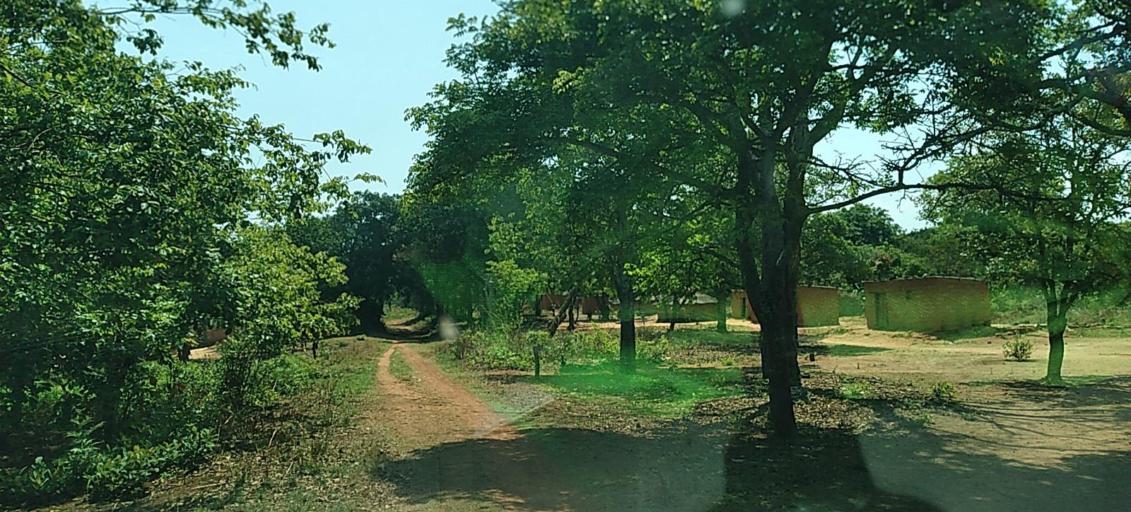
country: CD
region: Katanga
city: Kolwezi
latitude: -11.2821
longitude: 25.1448
